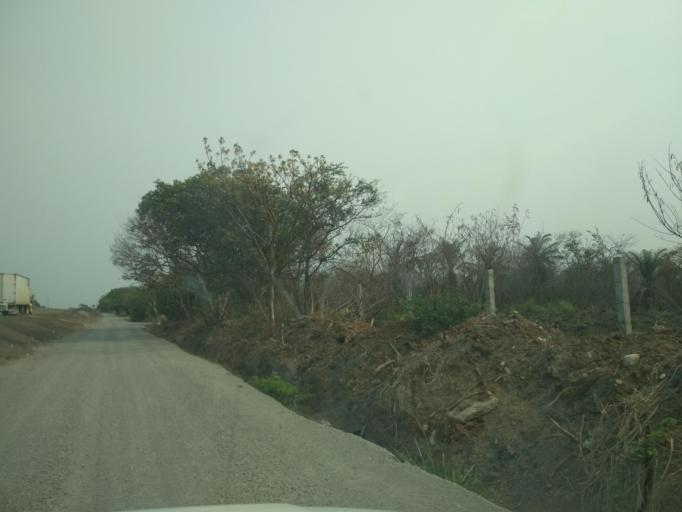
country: MX
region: Veracruz
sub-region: Veracruz
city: Hacienda Sotavento
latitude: 19.1045
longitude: -96.2196
